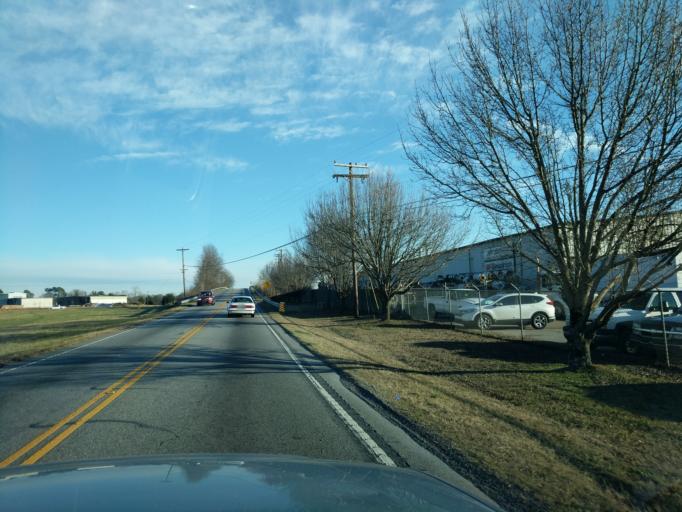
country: US
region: South Carolina
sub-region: Anderson County
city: Williamston
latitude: 34.6672
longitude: -82.5184
